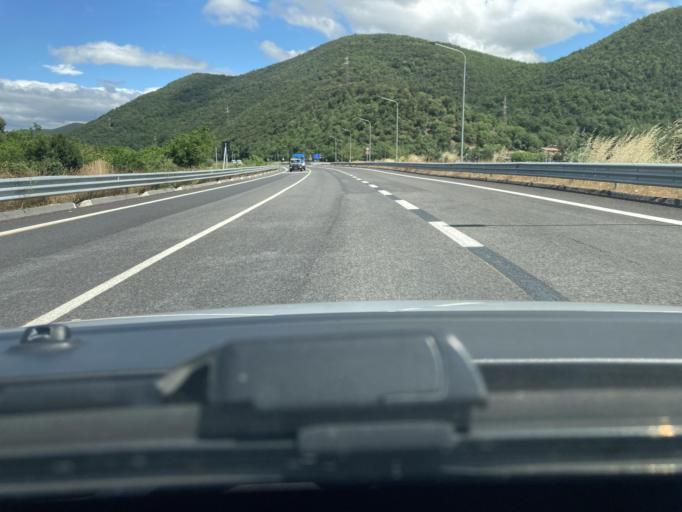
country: IT
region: Latium
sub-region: Provincia di Rieti
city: Colli sul Velino
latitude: 42.5072
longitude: 12.7469
